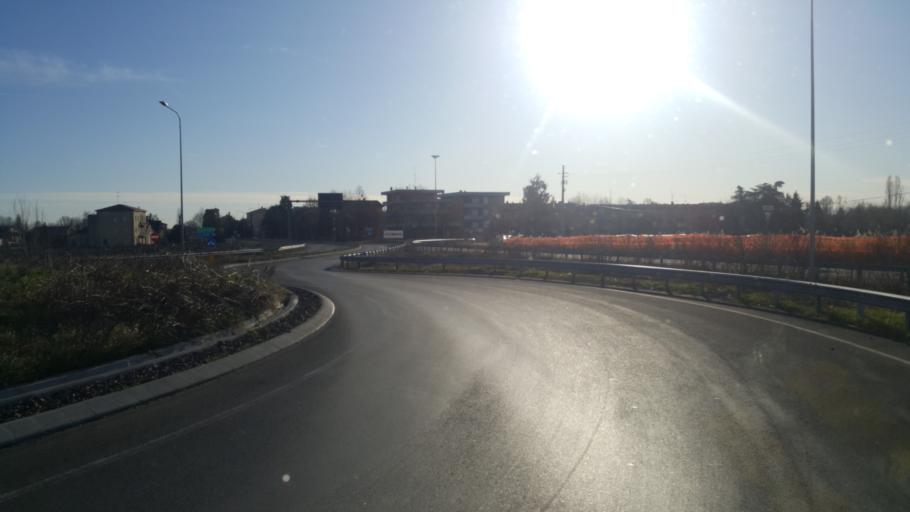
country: IT
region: Emilia-Romagna
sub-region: Provincia di Modena
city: Campogalliano
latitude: 44.6484
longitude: 10.8374
